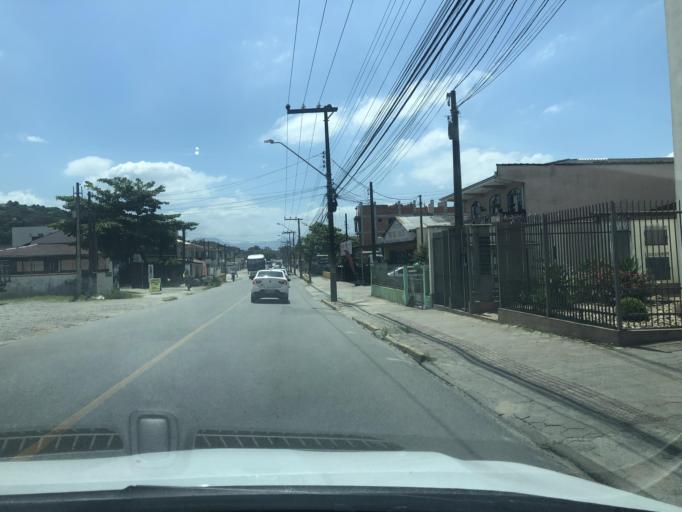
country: BR
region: Santa Catarina
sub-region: Joinville
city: Joinville
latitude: -26.3329
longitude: -48.8185
